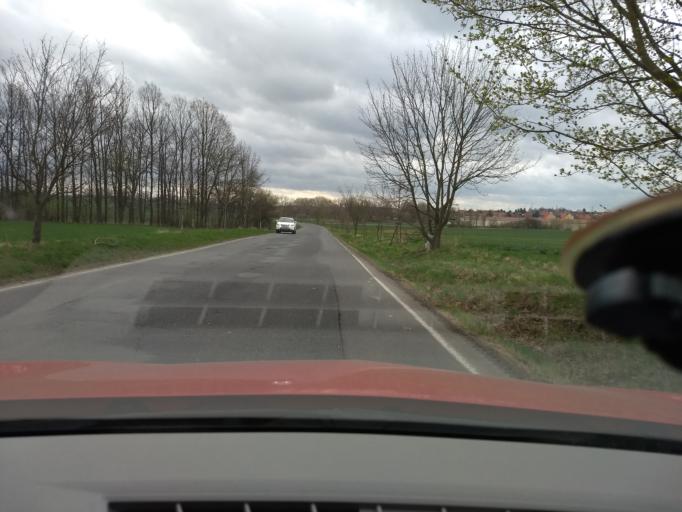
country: CZ
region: Central Bohemia
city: Unhost'
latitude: 50.0750
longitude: 14.1500
